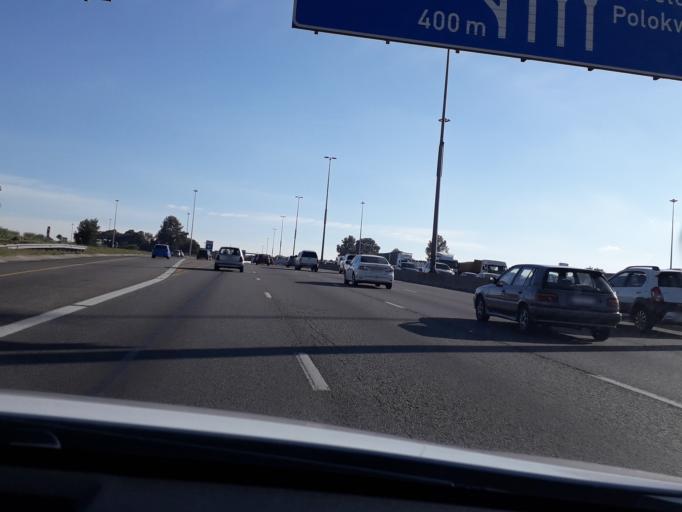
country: ZA
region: Gauteng
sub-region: City of Tshwane Metropolitan Municipality
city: Centurion
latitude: -25.9100
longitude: 28.1568
